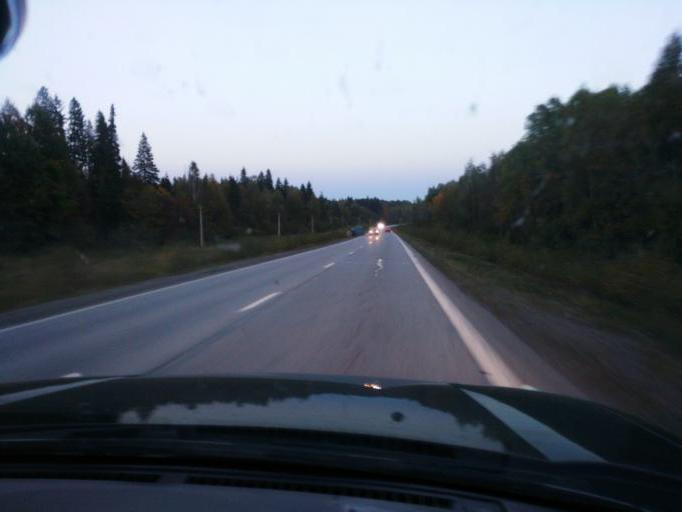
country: RU
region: Perm
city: Verkhnechusovskiye Gorodki
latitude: 58.2577
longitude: 56.9926
